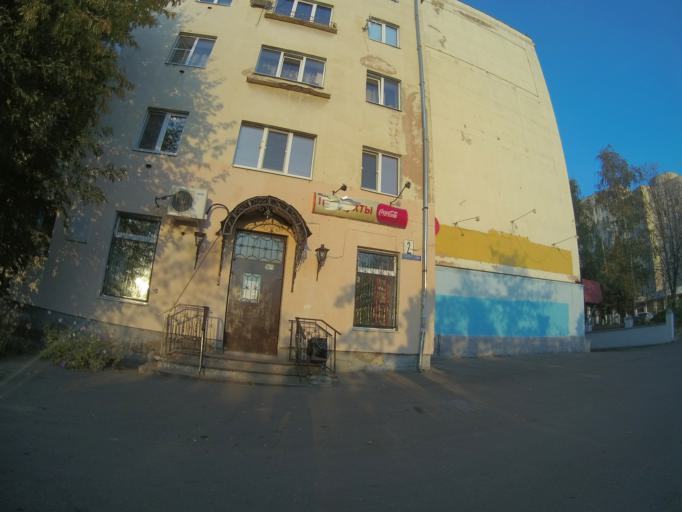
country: RU
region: Vladimir
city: Vladimir
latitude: 56.1165
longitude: 40.3436
